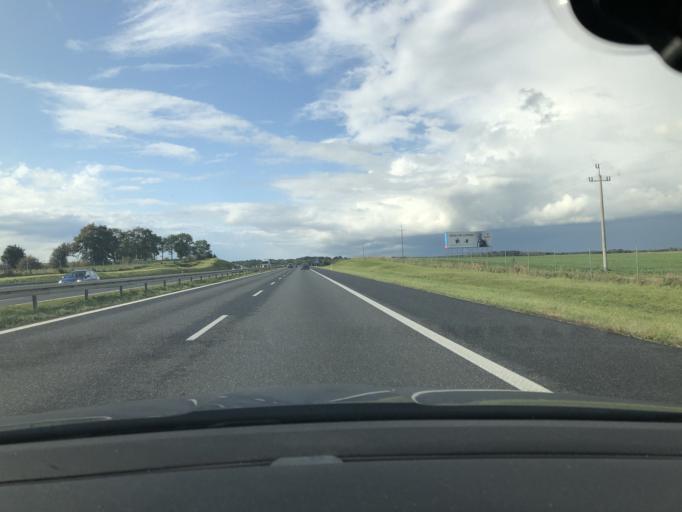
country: PL
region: Opole Voivodeship
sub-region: Powiat strzelecki
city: Ujazd
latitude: 50.4163
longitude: 18.4038
